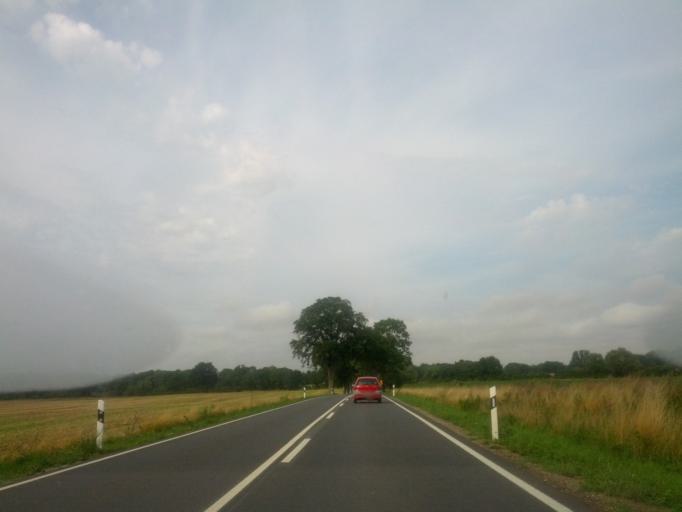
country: DE
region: Mecklenburg-Vorpommern
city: Sellin
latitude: 53.9325
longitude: 11.6045
